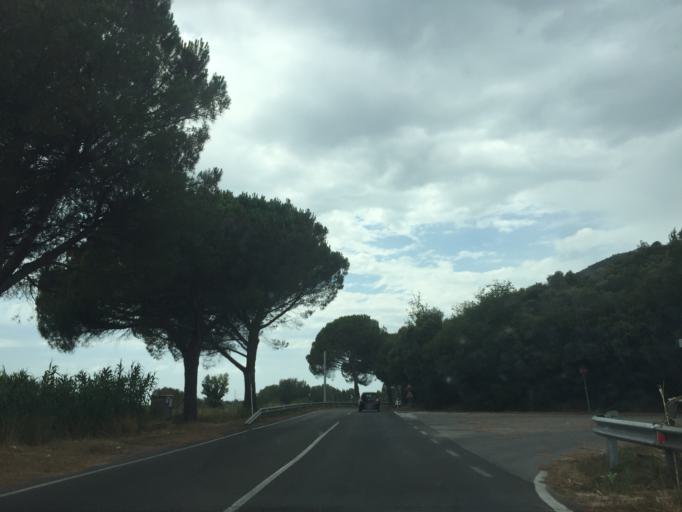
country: IT
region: Tuscany
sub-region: Province of Pisa
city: Asciano
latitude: 43.7505
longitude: 10.4545
